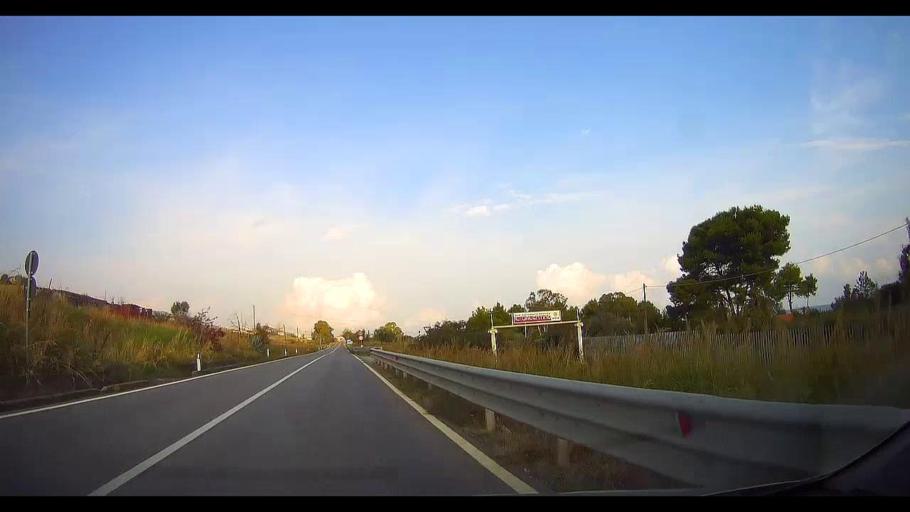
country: IT
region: Calabria
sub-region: Provincia di Cosenza
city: Cariati
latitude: 39.5197
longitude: 16.9052
